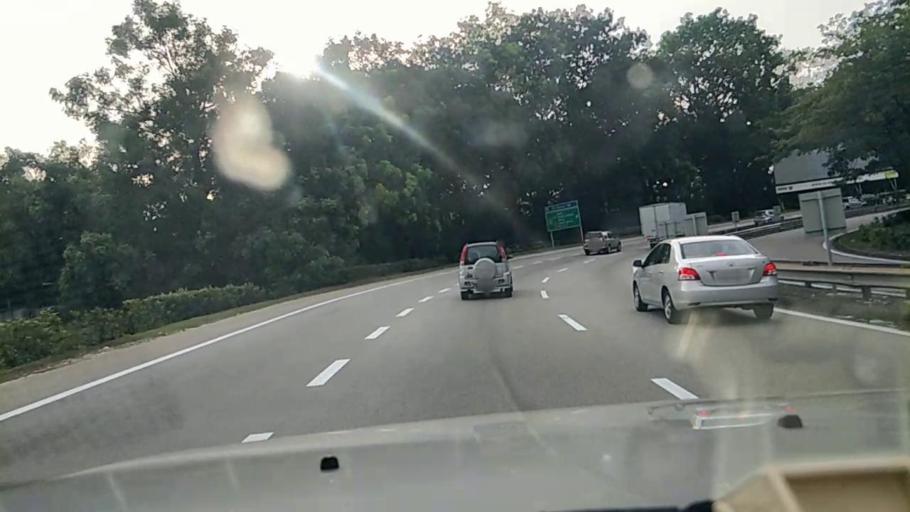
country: MY
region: Selangor
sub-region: Petaling
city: Petaling Jaya
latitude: 3.0987
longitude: 101.5880
